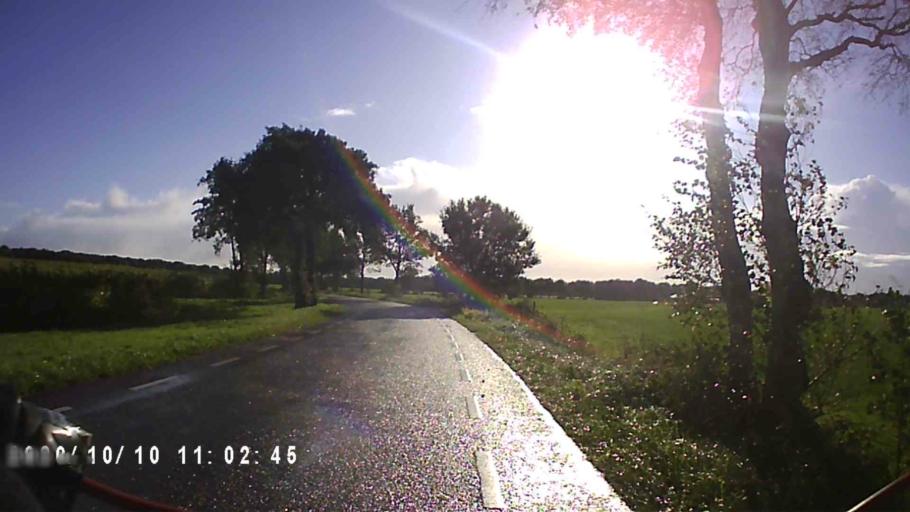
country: NL
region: Friesland
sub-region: Gemeente Achtkarspelen
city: Surhuisterveen
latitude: 53.1359
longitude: 6.2193
